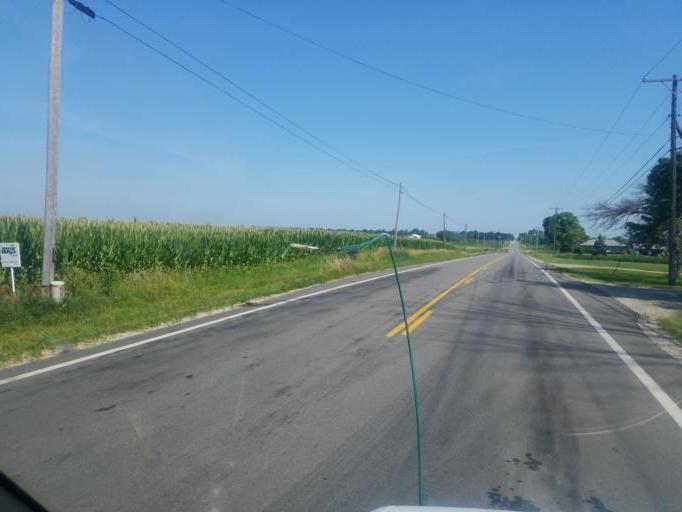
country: US
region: Ohio
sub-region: Union County
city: Marysville
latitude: 40.2927
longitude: -83.3797
